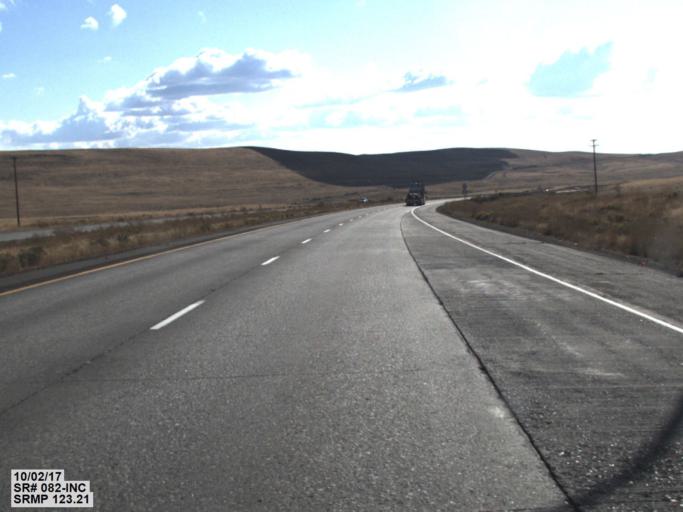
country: US
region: Oregon
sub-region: Umatilla County
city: Umatilla
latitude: 46.0187
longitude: -119.2264
